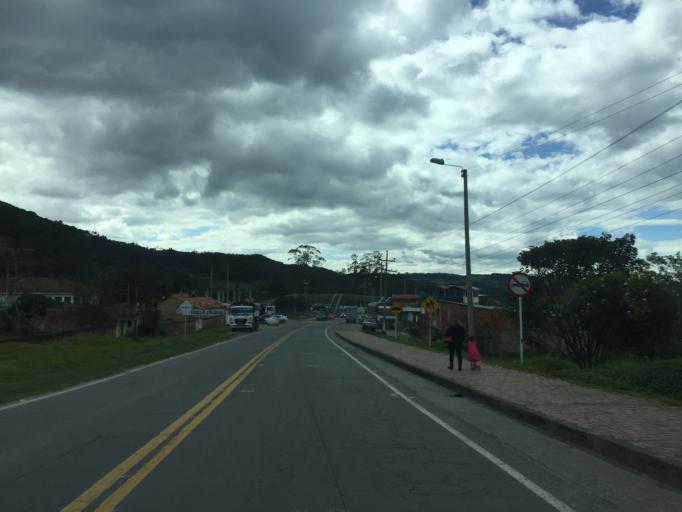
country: CO
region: Boyaca
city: Arcabuco
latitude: 5.7567
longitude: -73.4385
